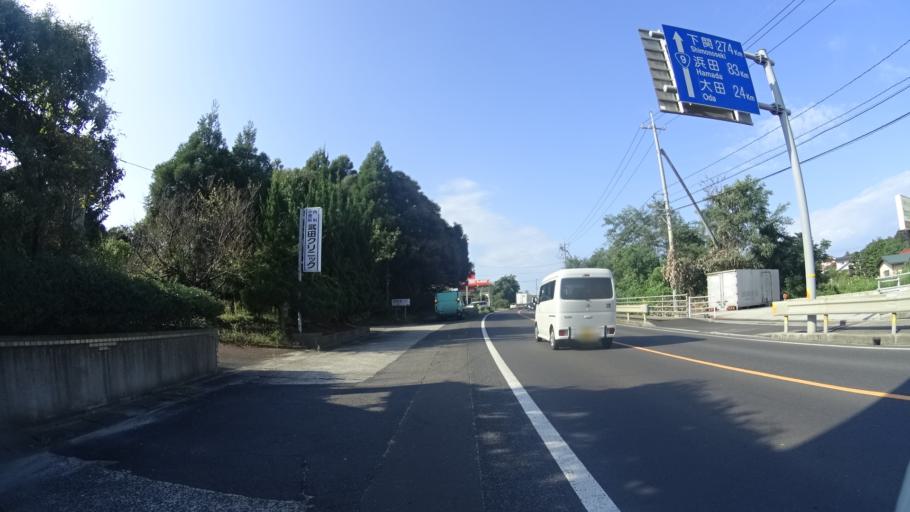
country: JP
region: Shimane
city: Izumo
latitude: 35.3262
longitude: 132.6735
